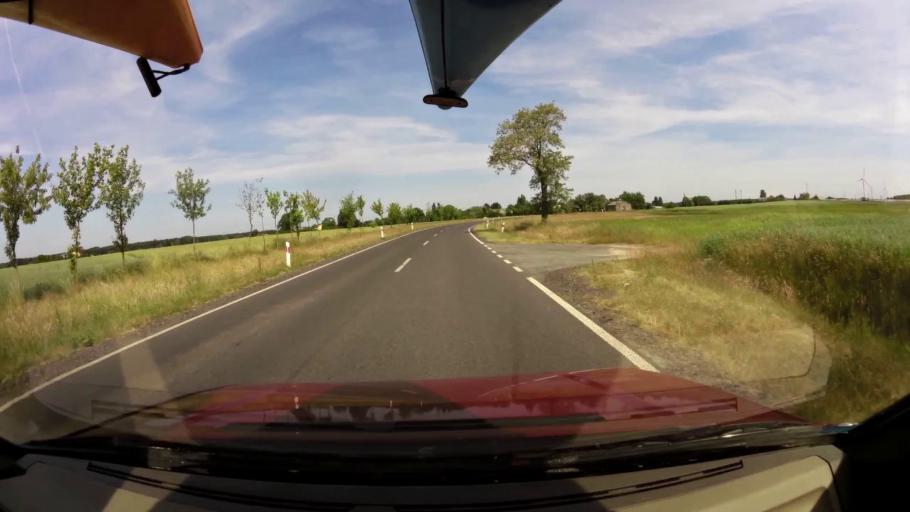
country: PL
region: West Pomeranian Voivodeship
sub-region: Powiat koszalinski
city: Sianow
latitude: 54.3059
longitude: 16.3067
